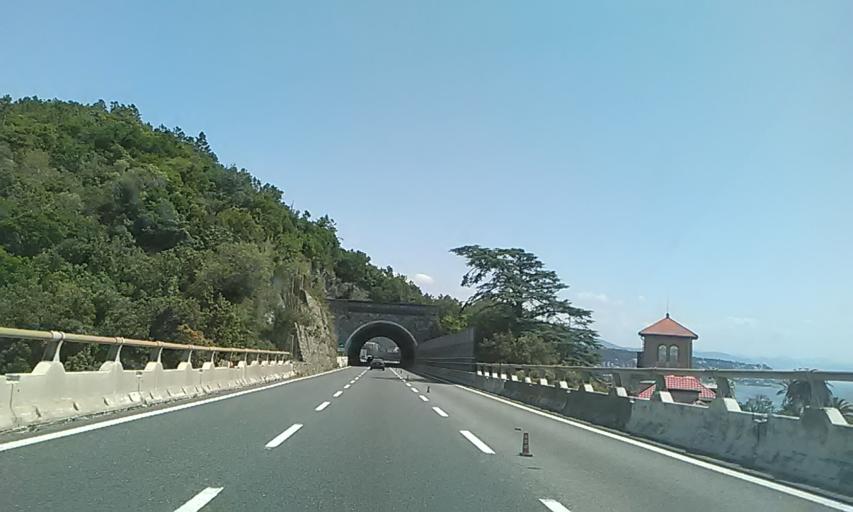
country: IT
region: Liguria
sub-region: Provincia di Genova
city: Cogoleto
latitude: 44.3818
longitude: 8.6312
